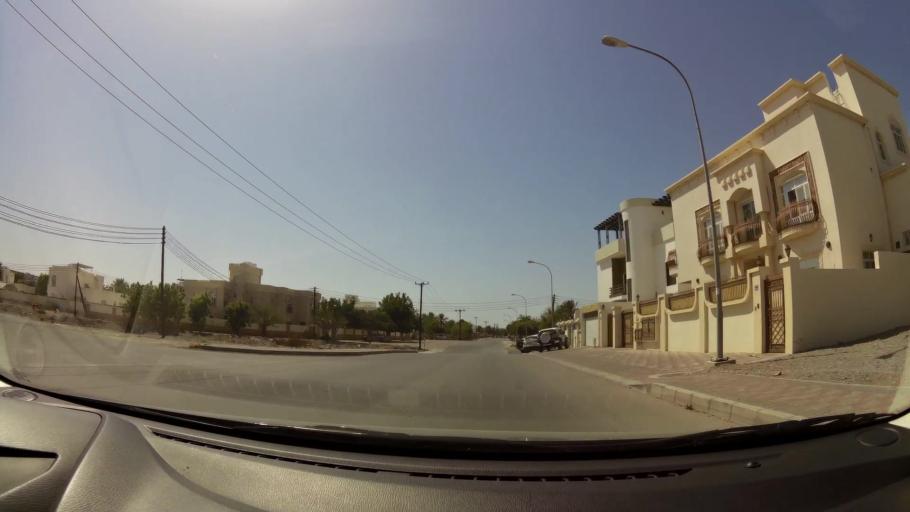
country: OM
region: Muhafazat Masqat
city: As Sib al Jadidah
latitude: 23.6329
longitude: 58.2202
